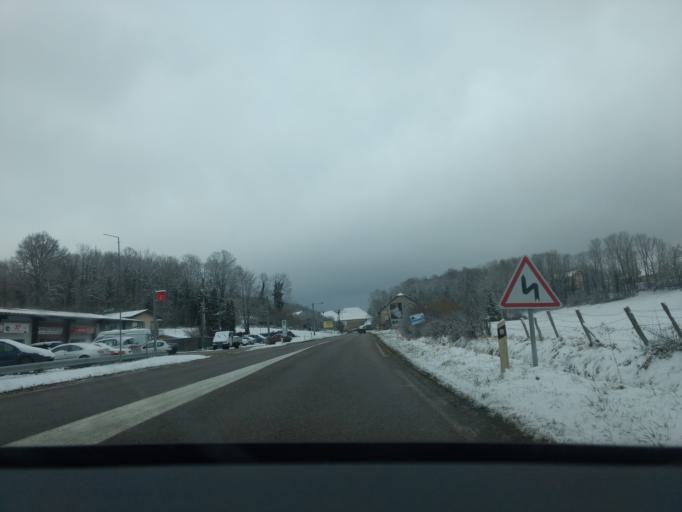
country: FR
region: Franche-Comte
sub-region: Departement du Jura
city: Champagnole
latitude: 46.8026
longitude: 5.8310
